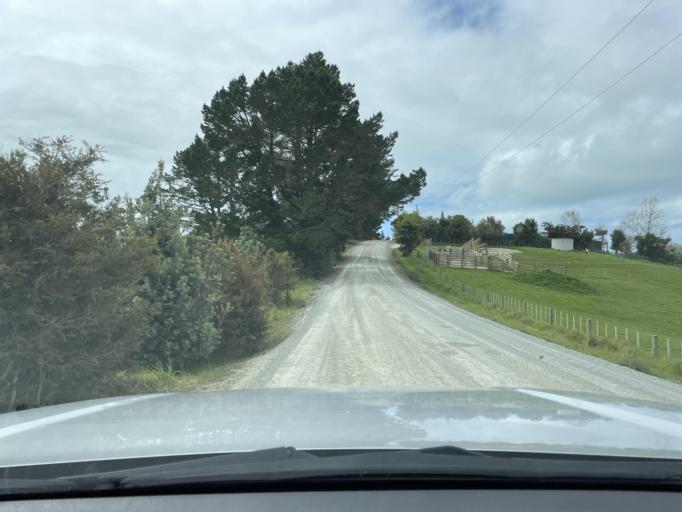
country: NZ
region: Auckland
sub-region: Auckland
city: Wellsford
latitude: -36.1716
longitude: 174.5786
